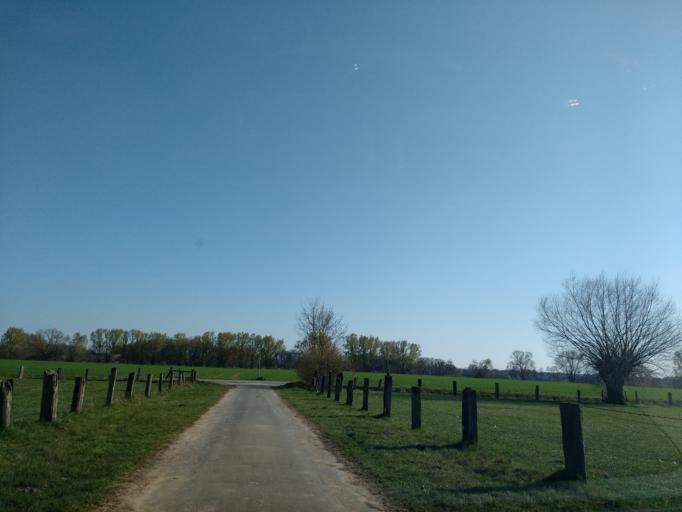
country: DE
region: North Rhine-Westphalia
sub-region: Regierungsbezirk Detmold
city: Delbruck
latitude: 51.7232
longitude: 8.5517
